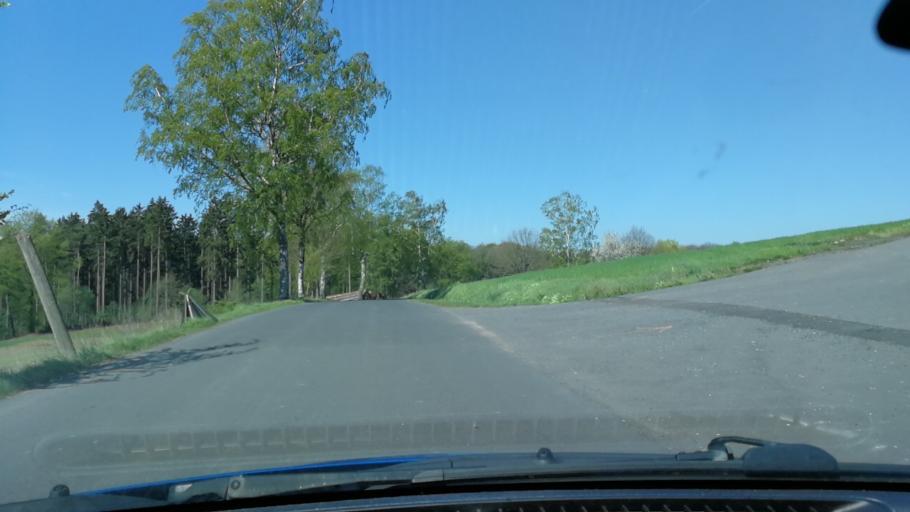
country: DE
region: Lower Saxony
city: Adelebsen
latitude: 51.6363
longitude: 9.7708
